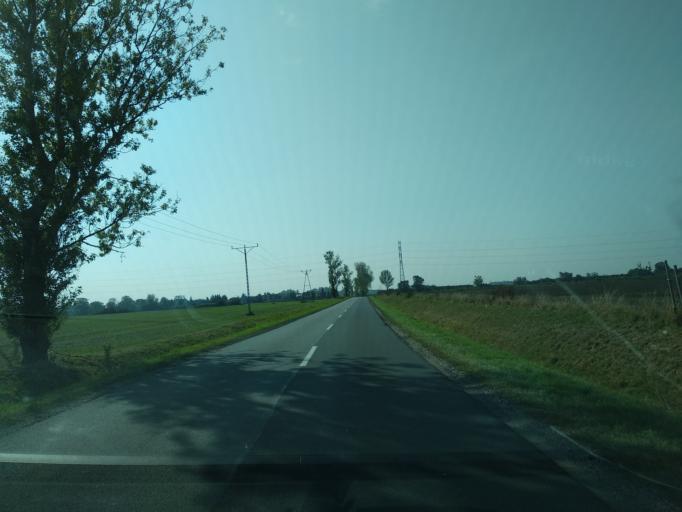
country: PL
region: Lower Silesian Voivodeship
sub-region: Powiat wroclawski
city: Zerniki Wroclawskie
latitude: 51.0412
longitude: 17.0298
